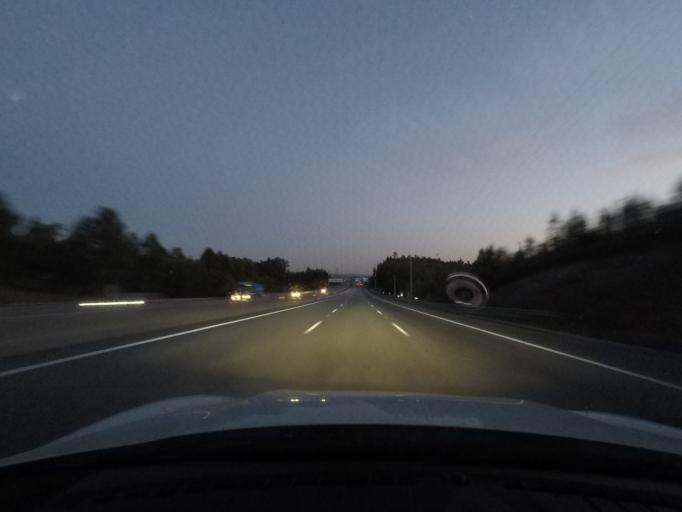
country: PT
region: Porto
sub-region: Gondomar
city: Foz do Sousa
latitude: 41.0837
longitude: -8.4542
